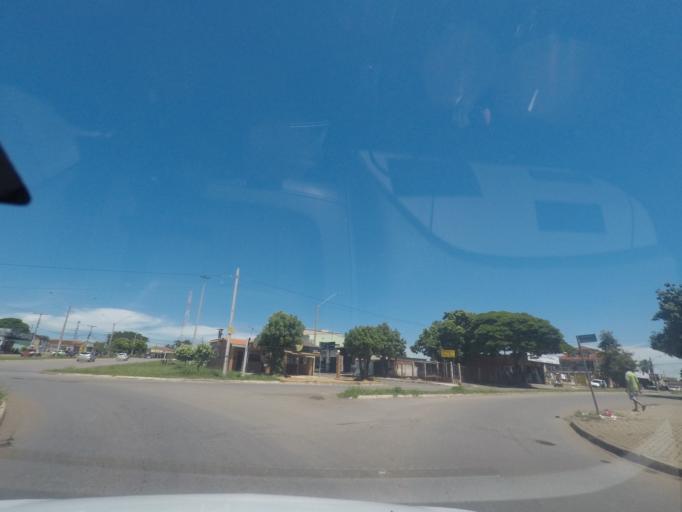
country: BR
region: Goias
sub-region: Aparecida De Goiania
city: Aparecida de Goiania
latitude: -16.7694
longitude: -49.3232
